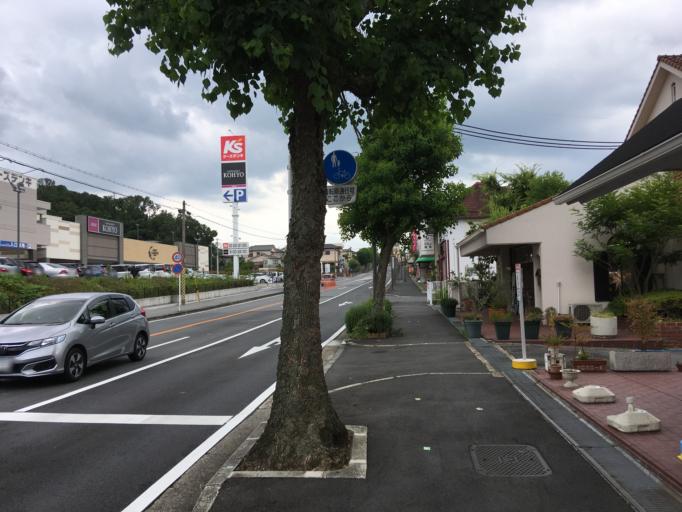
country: JP
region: Nara
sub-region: Ikoma-shi
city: Ikoma
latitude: 34.6859
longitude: 135.7157
